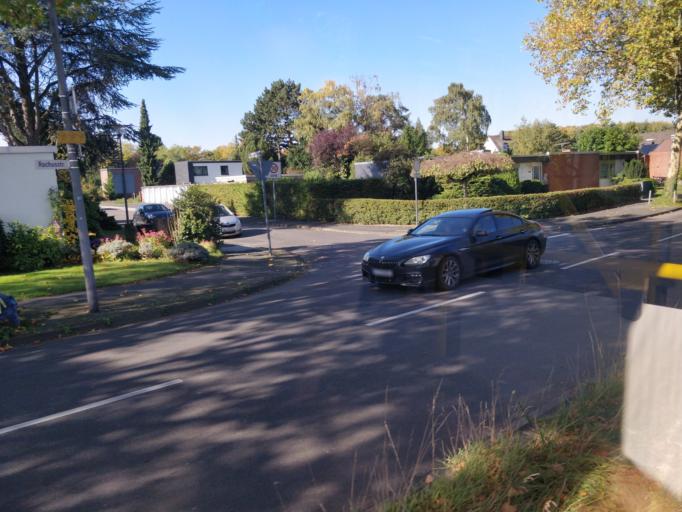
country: DE
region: North Rhine-Westphalia
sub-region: Regierungsbezirk Koln
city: Bilderstoeckchen
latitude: 50.9747
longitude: 6.9045
